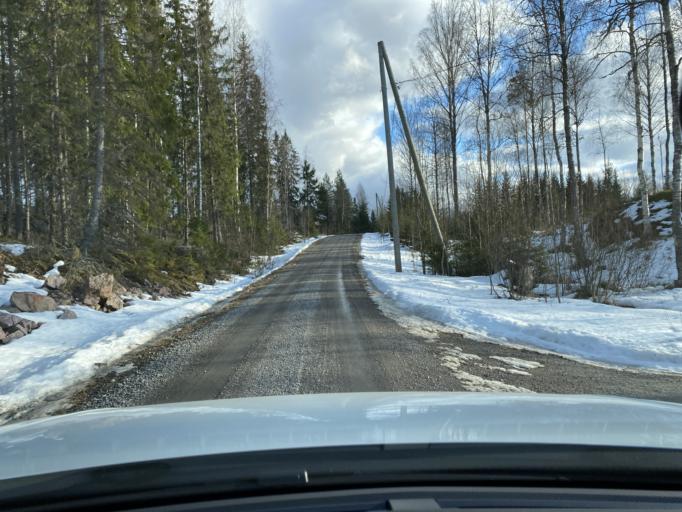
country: FI
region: Pirkanmaa
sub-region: Lounais-Pirkanmaa
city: Mouhijaervi
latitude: 61.4476
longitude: 22.9602
